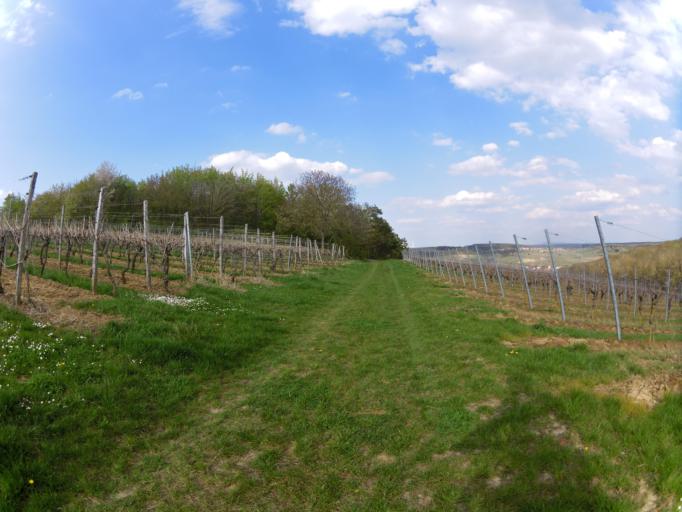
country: DE
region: Bavaria
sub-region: Regierungsbezirk Unterfranken
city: Winterhausen
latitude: 49.6961
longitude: 10.0104
